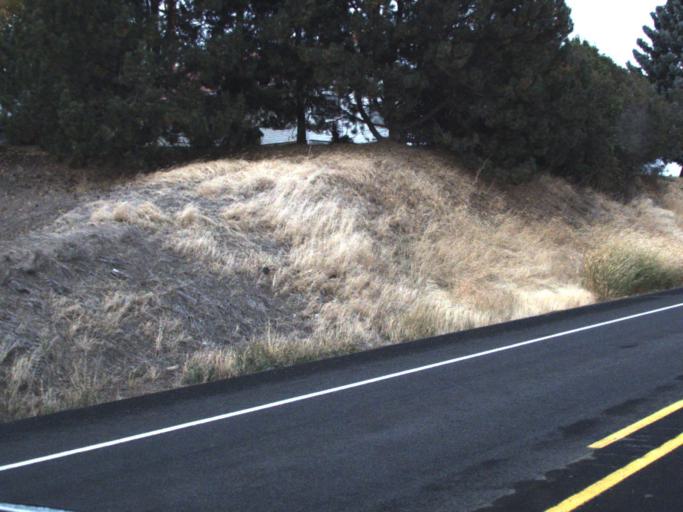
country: US
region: Washington
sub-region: Whitman County
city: Pullman
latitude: 46.6989
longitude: -117.2039
